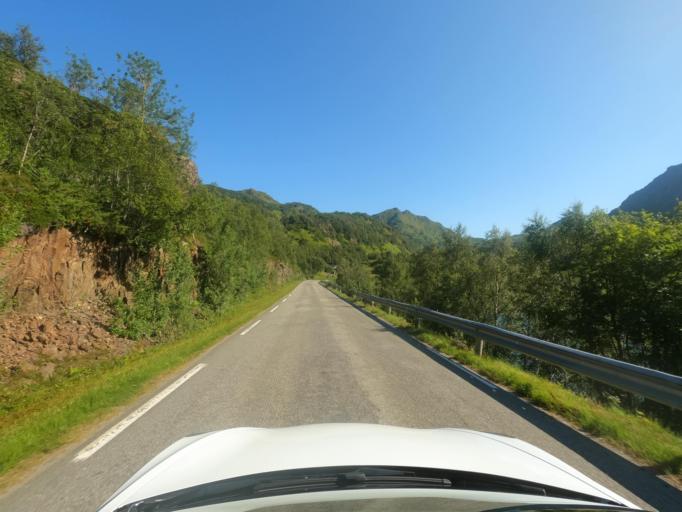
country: NO
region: Nordland
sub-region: Hadsel
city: Stokmarknes
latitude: 68.3570
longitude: 15.0686
